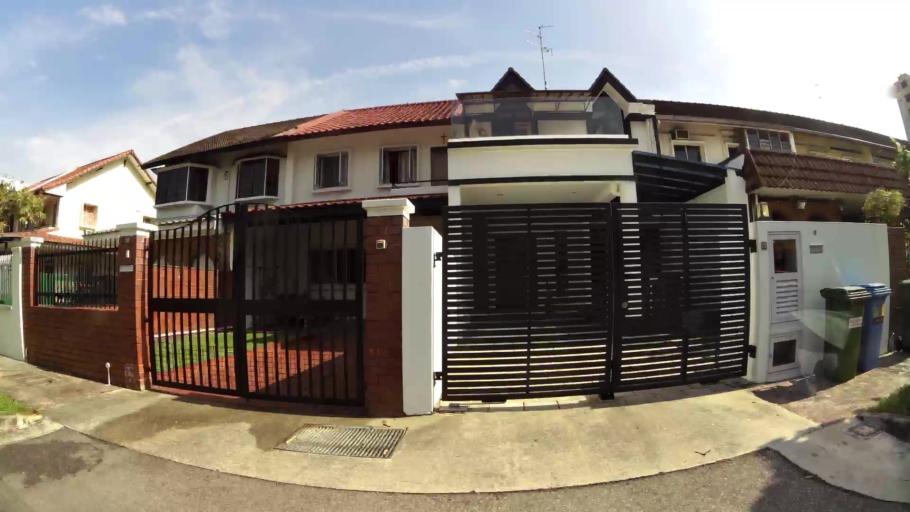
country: SG
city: Singapore
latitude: 1.3556
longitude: 103.8357
